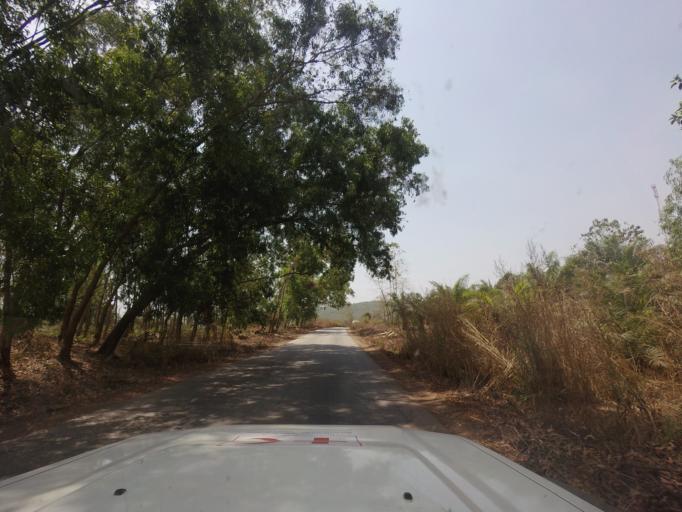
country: GN
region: Kindia
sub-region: Kindia
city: Kindia
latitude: 9.9100
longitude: -12.9957
